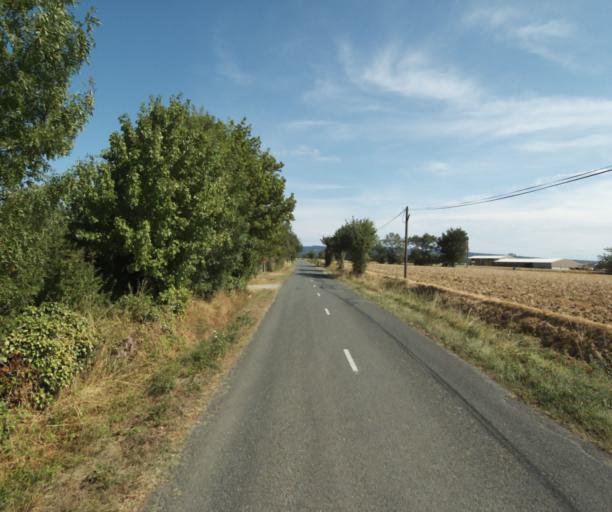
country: FR
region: Midi-Pyrenees
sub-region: Departement de la Haute-Garonne
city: Revel
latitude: 43.4880
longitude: 1.9866
